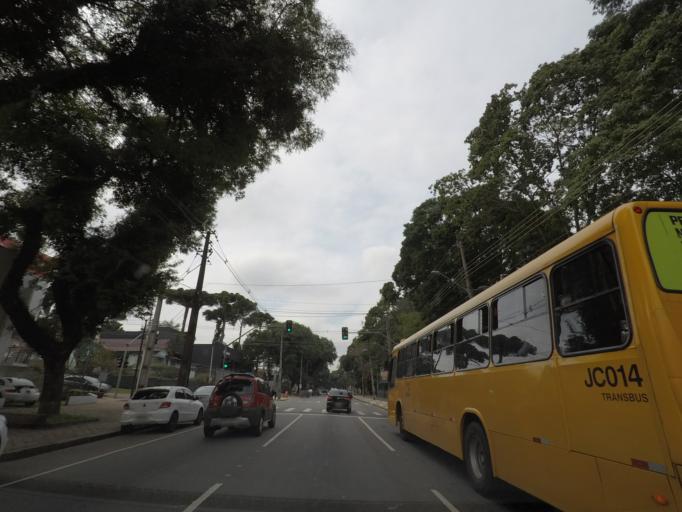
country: BR
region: Parana
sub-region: Curitiba
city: Curitiba
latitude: -25.4465
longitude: -49.2760
